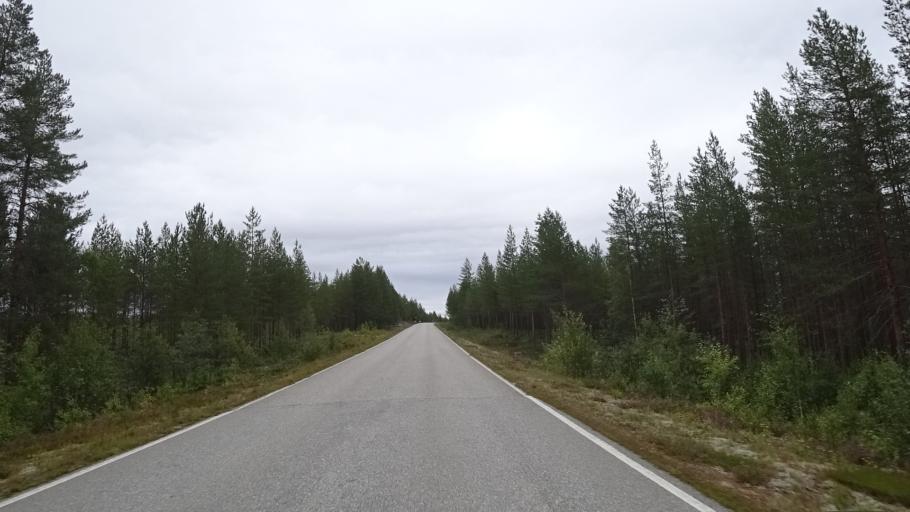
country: FI
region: North Karelia
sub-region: Pielisen Karjala
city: Lieksa
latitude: 63.3807
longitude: 30.3192
